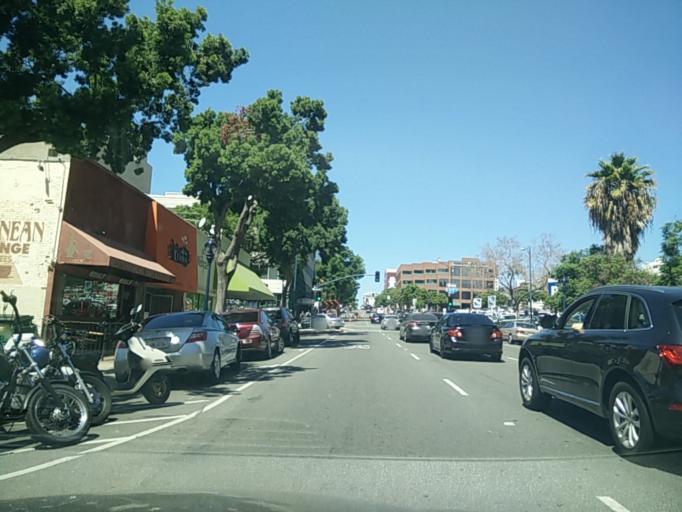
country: US
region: California
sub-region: San Diego County
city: San Diego
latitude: 32.7193
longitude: -117.1602
